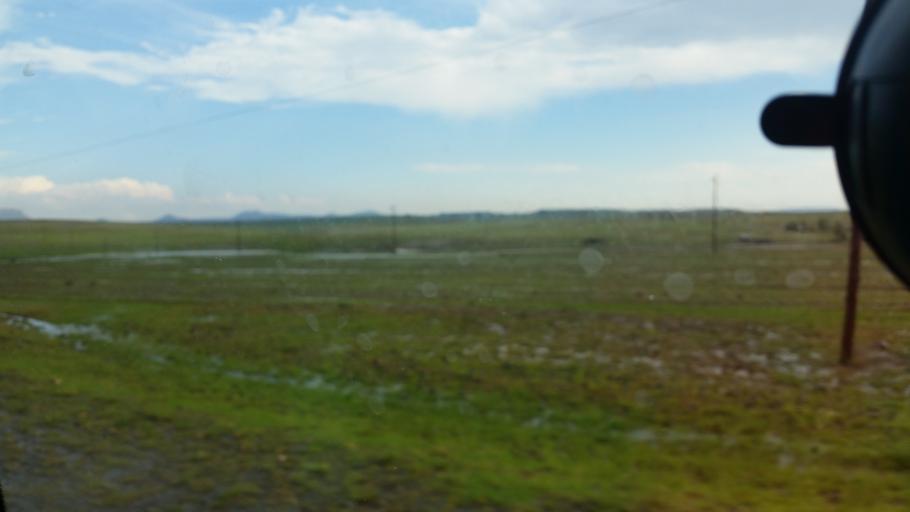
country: LS
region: Mafeteng
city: Mafeteng
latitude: -29.7733
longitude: 27.1895
